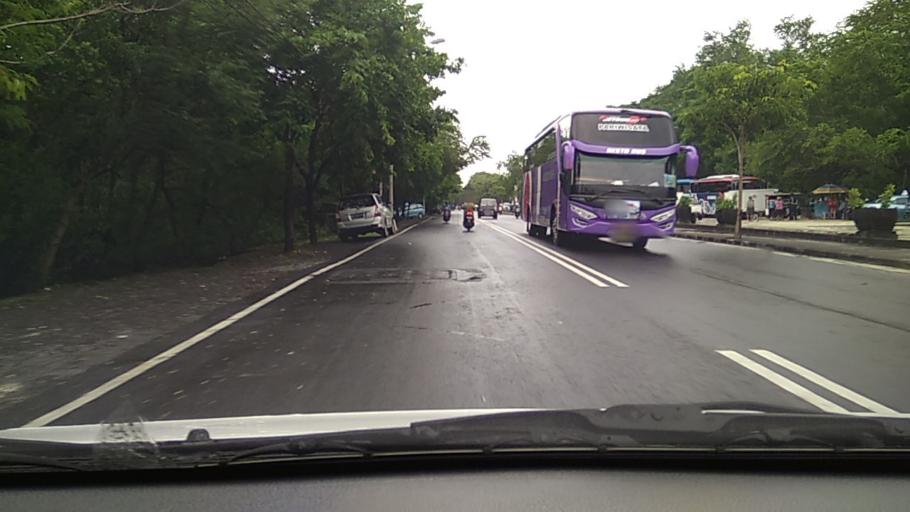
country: ID
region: Bali
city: Bualu
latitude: -8.7905
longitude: 115.2202
